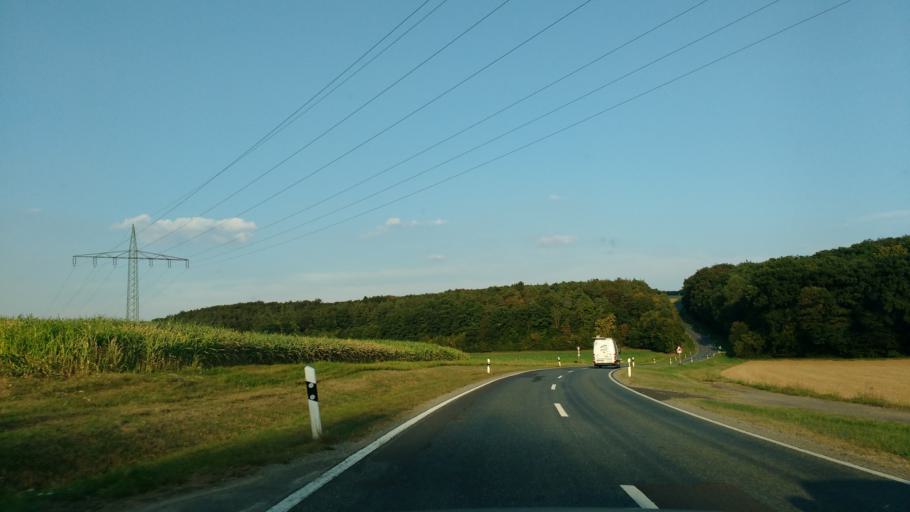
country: DE
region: Bavaria
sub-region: Regierungsbezirk Unterfranken
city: Wasserlosen
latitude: 50.0826
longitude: 9.9951
